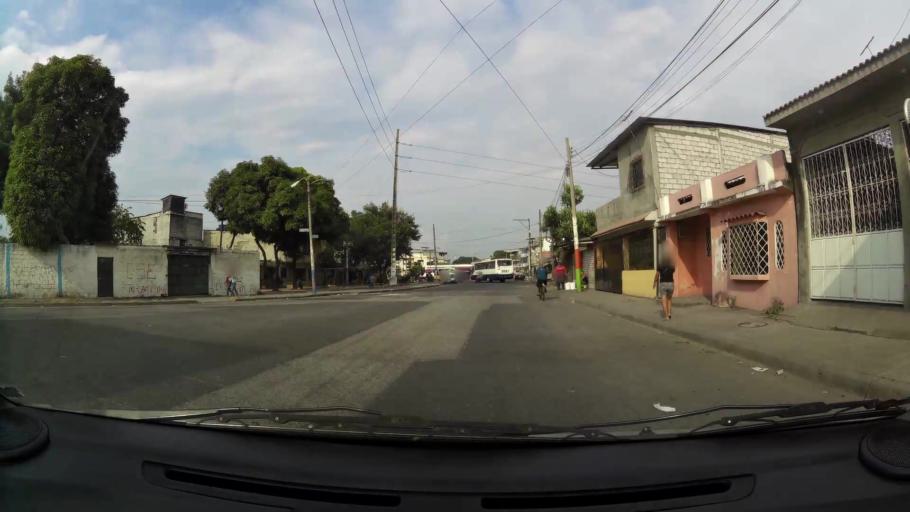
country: EC
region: Guayas
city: Guayaquil
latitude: -2.2510
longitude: -79.9044
